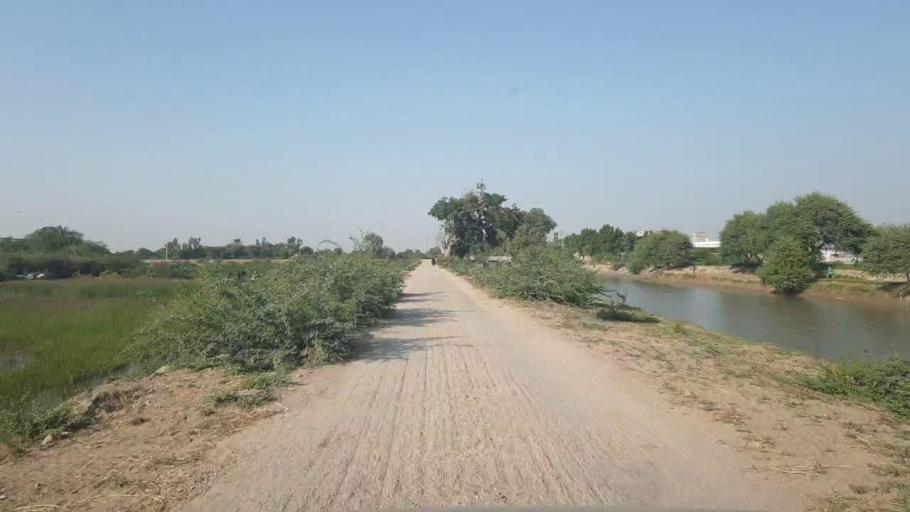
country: PK
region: Sindh
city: Badin
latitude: 24.6528
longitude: 68.8152
